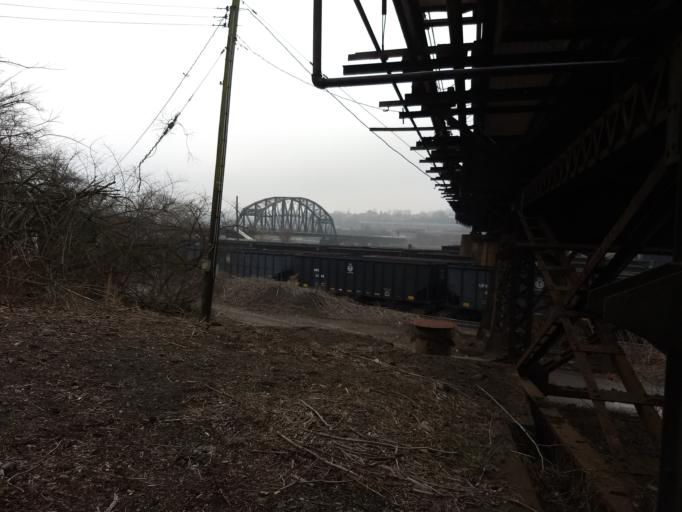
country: US
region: Pennsylvania
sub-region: Allegheny County
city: East Pittsburgh
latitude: 40.3903
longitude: -79.8493
